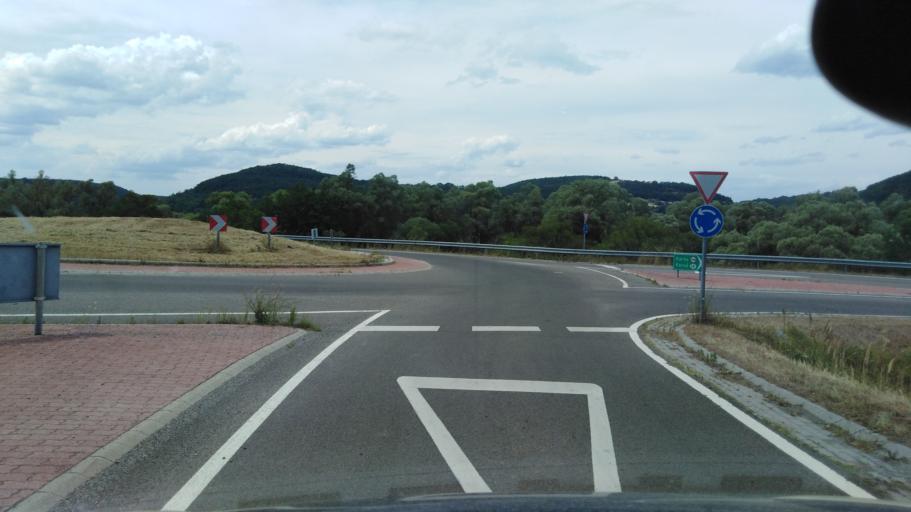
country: HU
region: Nograd
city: Szecseny
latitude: 48.2076
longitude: 19.5409
